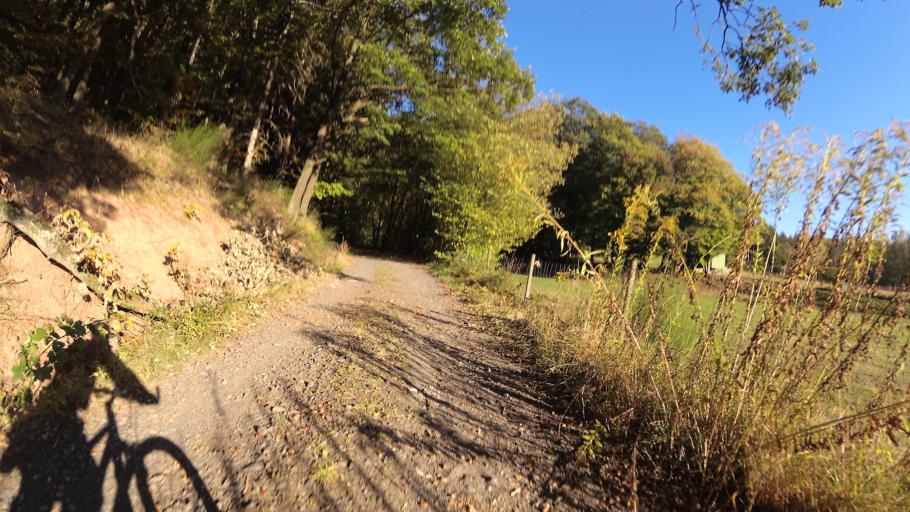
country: DE
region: Saarland
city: Sankt Wendel
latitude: 49.4332
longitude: 7.1798
